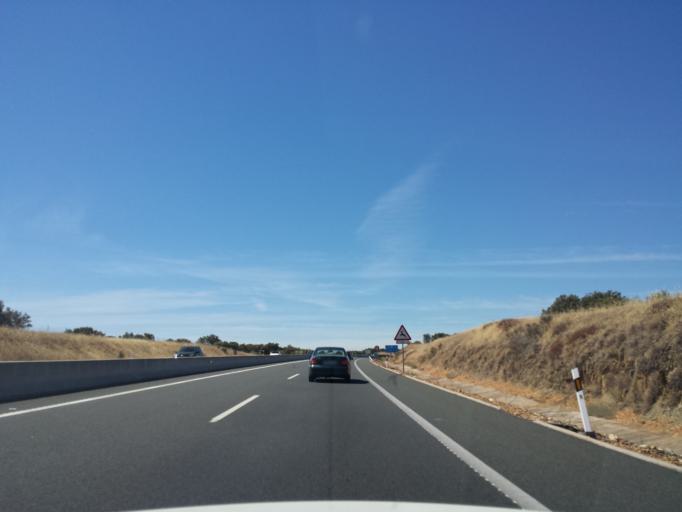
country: ES
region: Extremadura
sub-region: Provincia de Caceres
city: Jaraicejo
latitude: 39.6378
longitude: -5.8113
